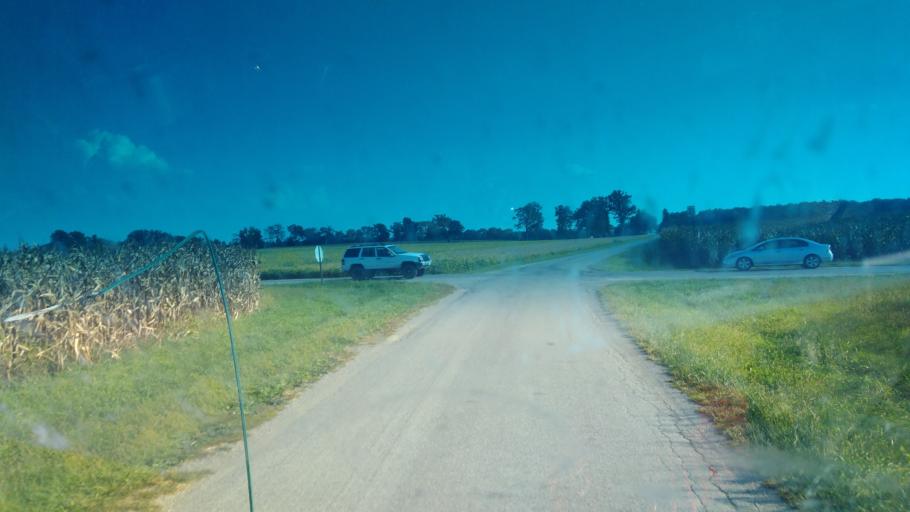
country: US
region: Ohio
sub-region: Wyandot County
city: Upper Sandusky
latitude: 40.8918
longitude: -83.2425
